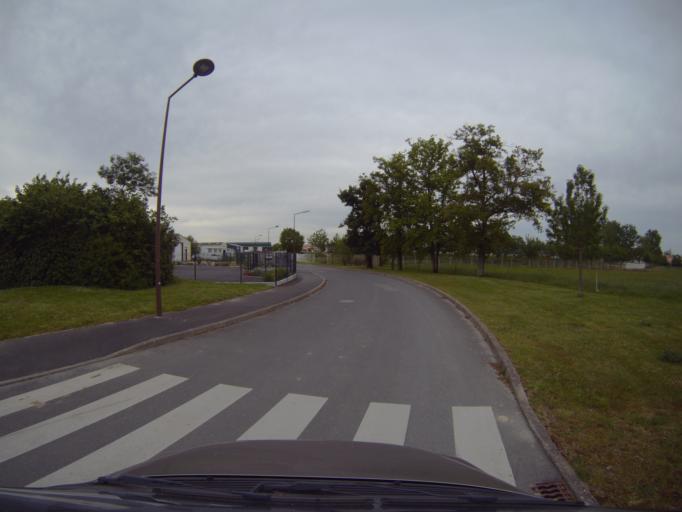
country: FR
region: Pays de la Loire
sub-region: Departement de la Loire-Atlantique
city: La Planche
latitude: 47.0205
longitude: -1.4267
